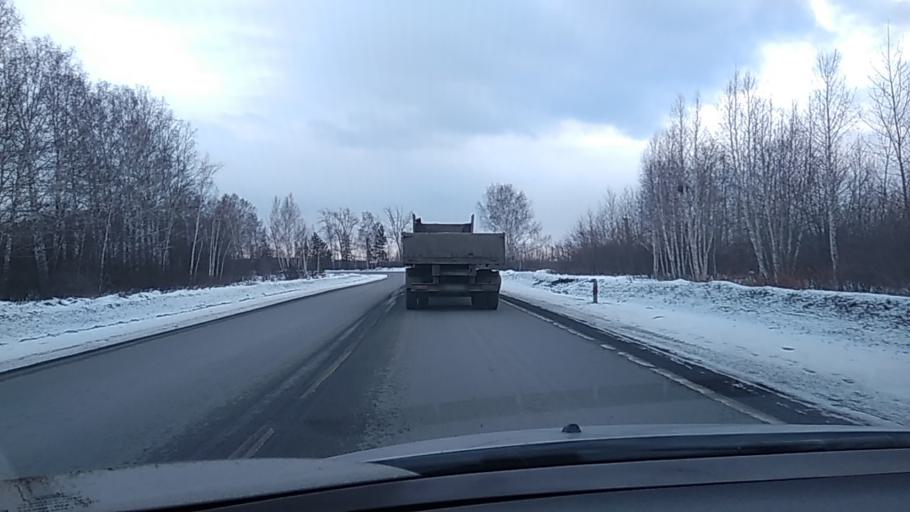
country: RU
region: Sverdlovsk
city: Sovkhoznyy
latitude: 56.5963
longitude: 61.3029
